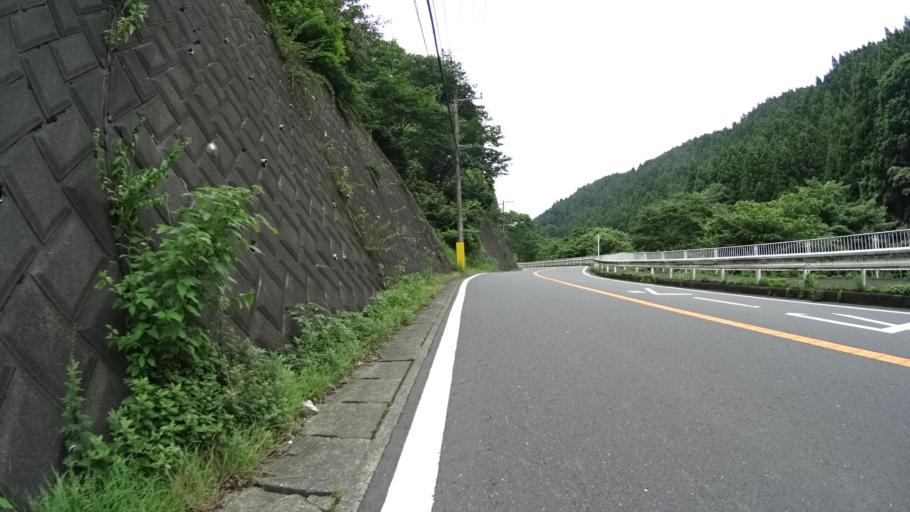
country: JP
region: Kanagawa
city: Atsugi
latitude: 35.4968
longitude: 139.2638
